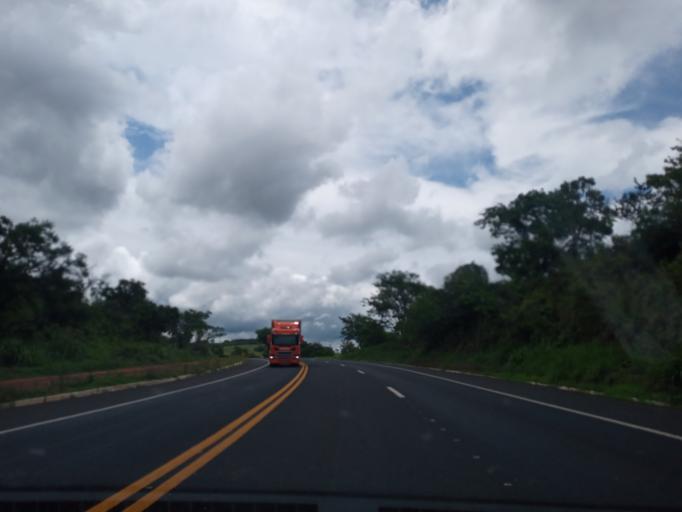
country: BR
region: Minas Gerais
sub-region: Monte Carmelo
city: Monte Carmelo
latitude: -19.2607
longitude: -47.6507
